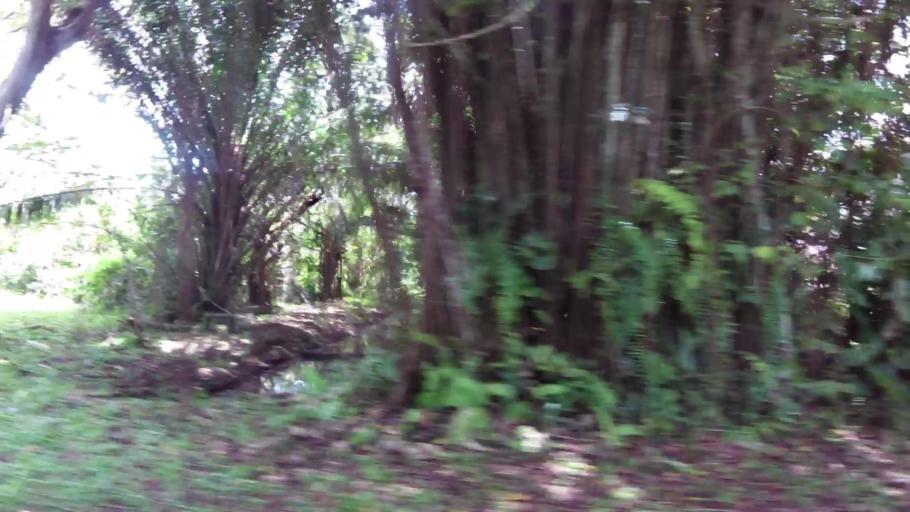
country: BN
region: Belait
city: Kuala Belait
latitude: 4.5946
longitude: 114.2570
